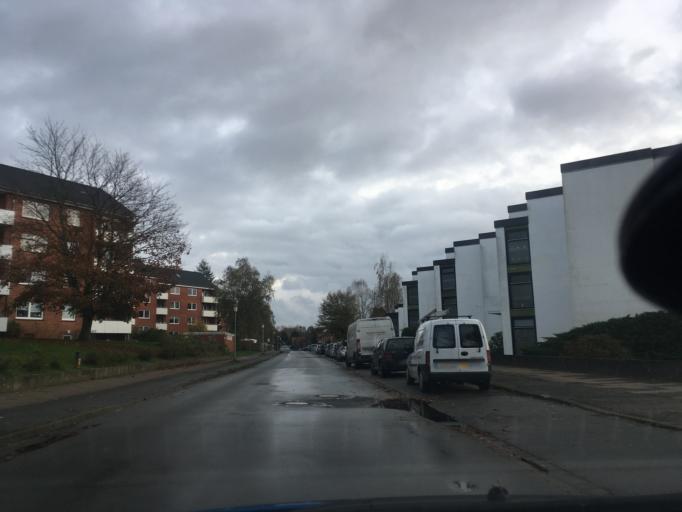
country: DE
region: Lower Saxony
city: Lueneburg
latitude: 53.2456
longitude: 10.4339
